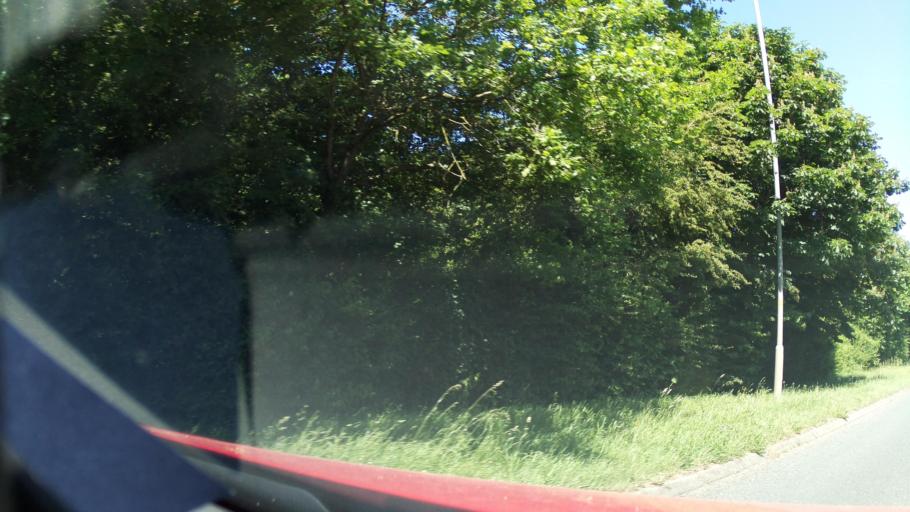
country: GB
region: England
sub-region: Wiltshire
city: Calne
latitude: 51.4466
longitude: -2.0171
